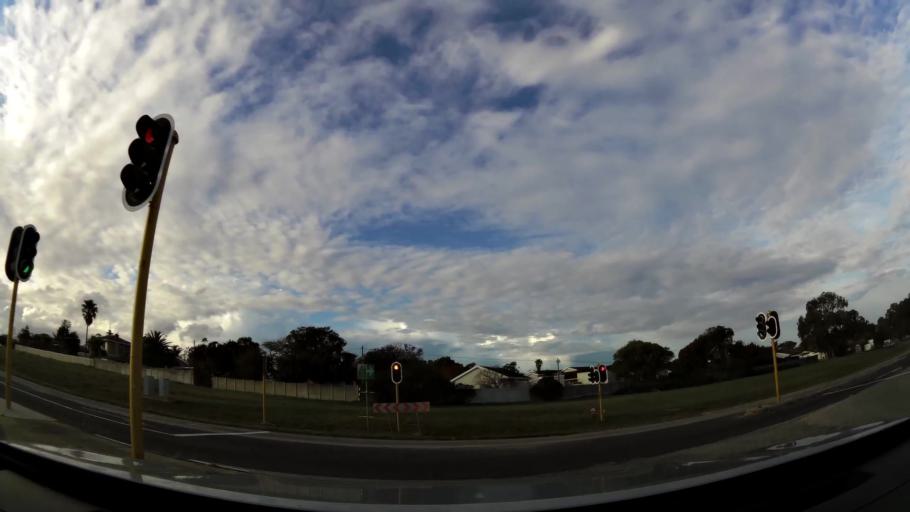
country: ZA
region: Eastern Cape
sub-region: Nelson Mandela Bay Metropolitan Municipality
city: Port Elizabeth
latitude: -33.9526
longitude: 25.5125
